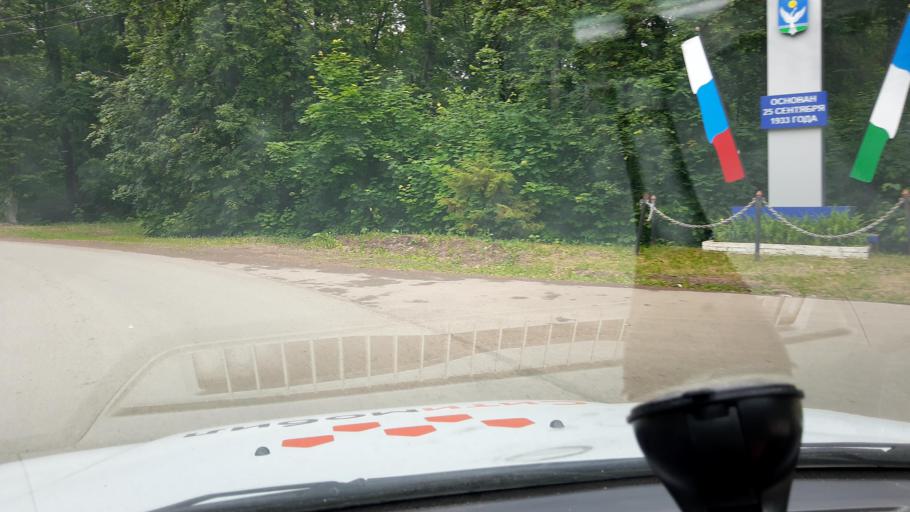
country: RU
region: Bashkortostan
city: Avdon
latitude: 54.6519
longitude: 55.5916
